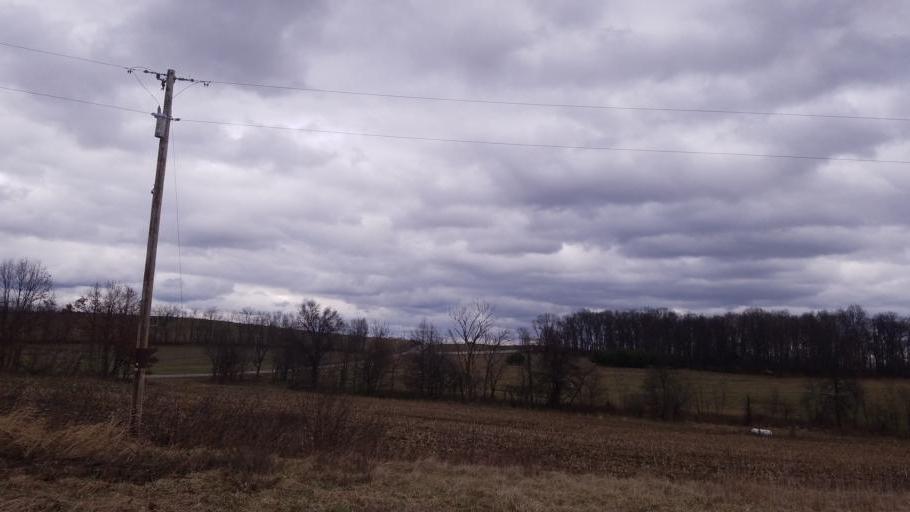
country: US
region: Ohio
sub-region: Licking County
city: Utica
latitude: 40.1963
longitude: -82.3835
